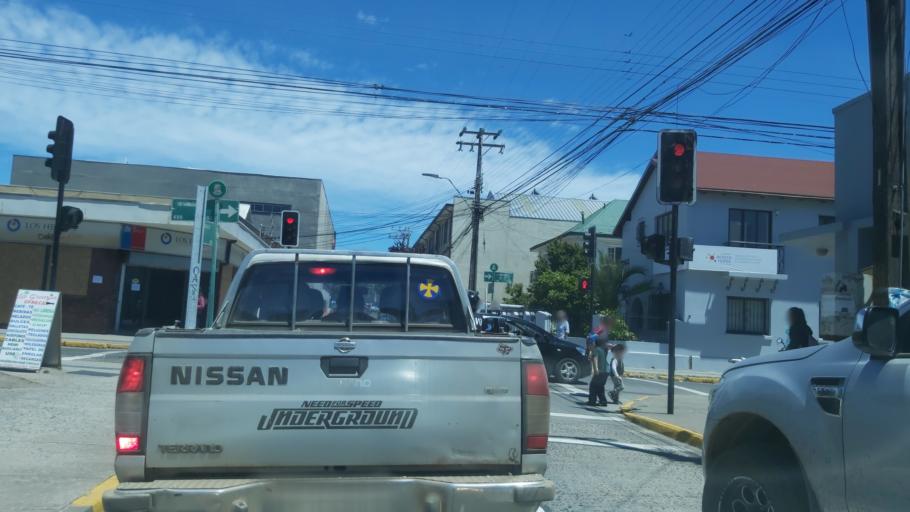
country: CL
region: Maule
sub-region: Provincia de Talca
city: Constitucion
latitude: -35.3295
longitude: -72.4108
